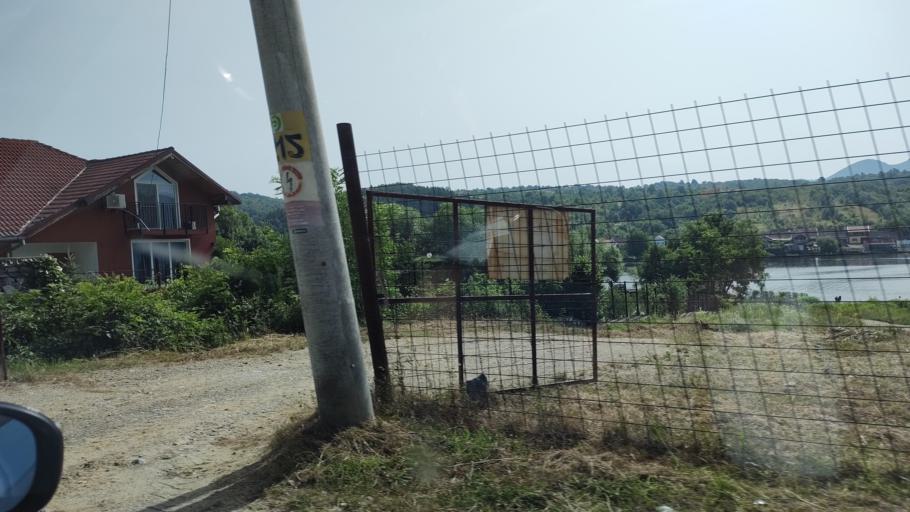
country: RO
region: Mehedinti
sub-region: Comuna Eselnita
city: Eselnita
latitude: 44.6899
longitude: 22.3634
